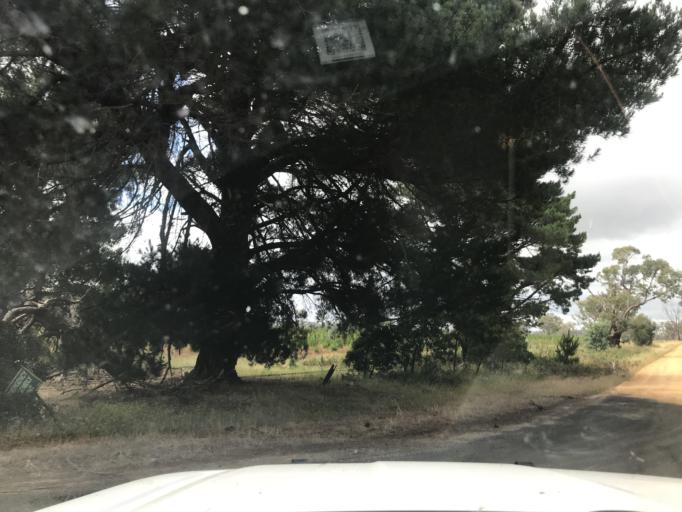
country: AU
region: South Australia
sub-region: Wattle Range
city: Penola
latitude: -37.2400
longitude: 141.0784
